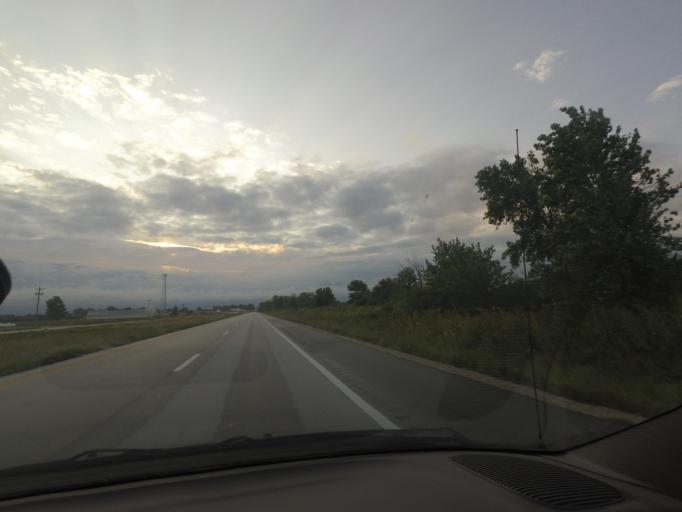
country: US
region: Missouri
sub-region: Shelby County
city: Shelbina
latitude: 39.6997
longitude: -92.0658
